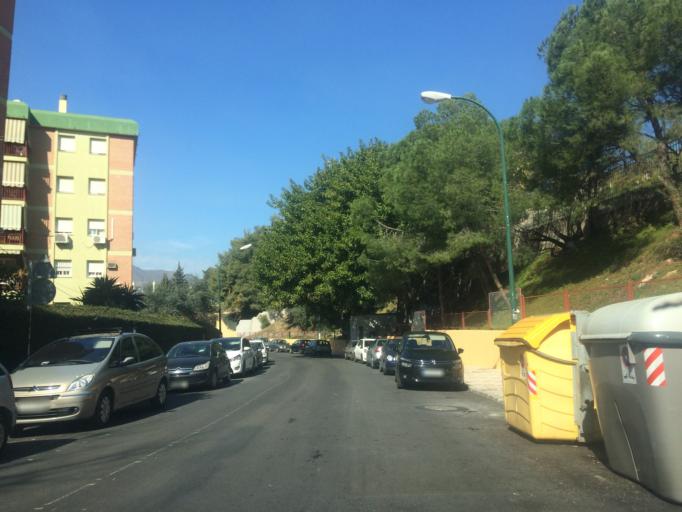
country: ES
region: Andalusia
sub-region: Provincia de Malaga
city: Malaga
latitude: 36.7502
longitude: -4.4151
